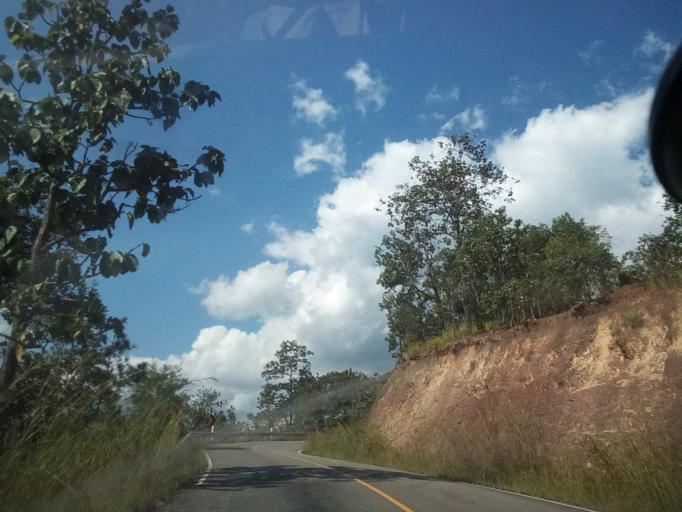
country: TH
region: Chiang Mai
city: Samoeng
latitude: 18.8701
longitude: 98.6913
